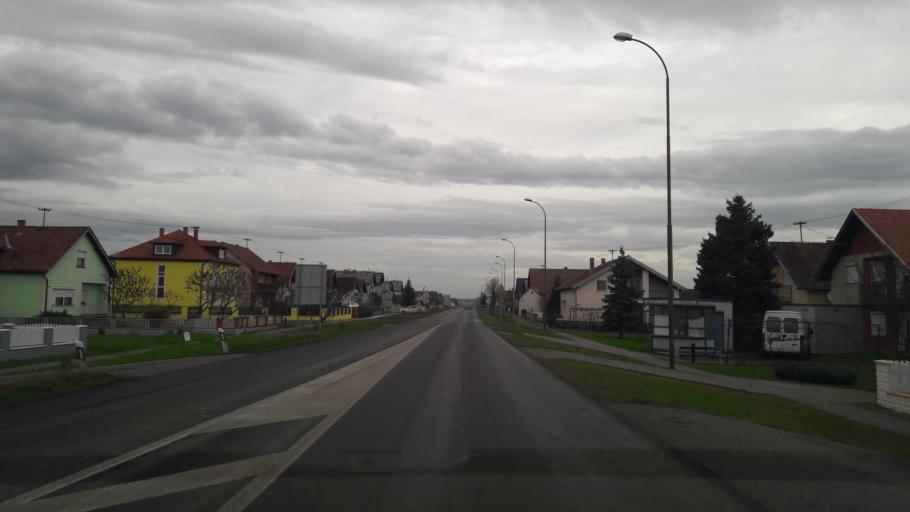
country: HR
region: Osjecko-Baranjska
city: Velimirovac
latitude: 45.5143
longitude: 18.0951
